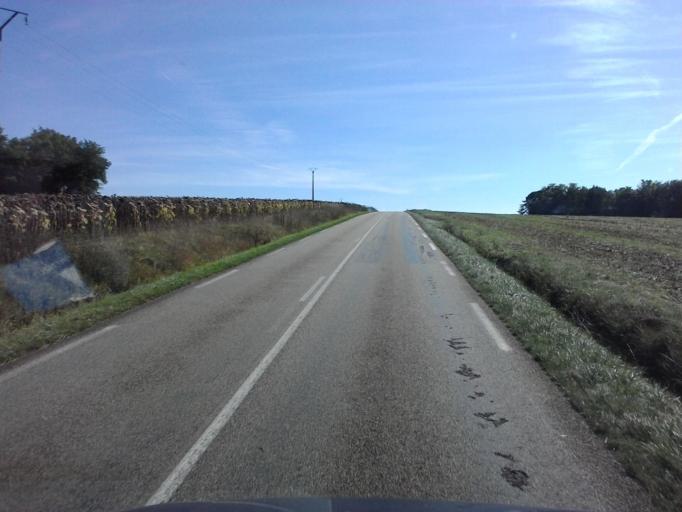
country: FR
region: Bourgogne
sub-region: Departement de l'Yonne
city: Joux-la-Ville
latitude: 47.5763
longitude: 3.8785
